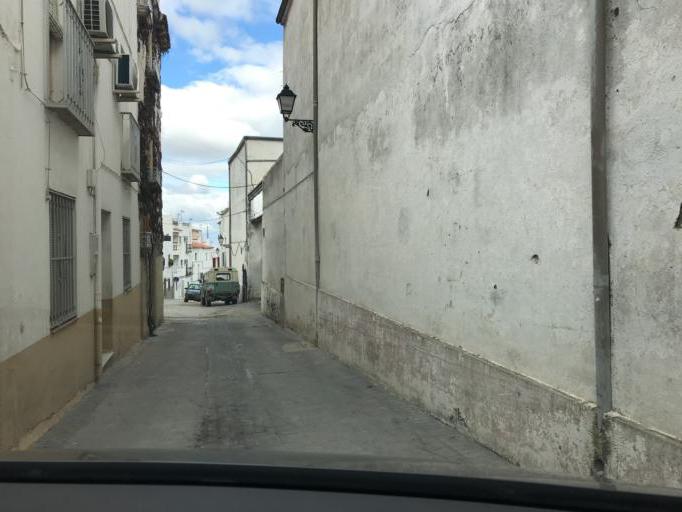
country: ES
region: Andalusia
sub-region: Provincia de Jaen
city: Torres
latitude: 37.7923
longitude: -3.4658
